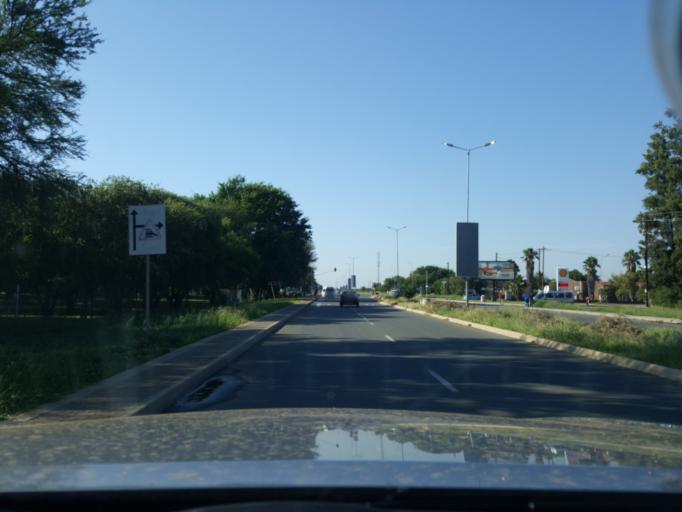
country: ZA
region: North-West
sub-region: Ngaka Modiri Molema District Municipality
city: Mmabatho
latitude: -25.8159
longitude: 25.6340
